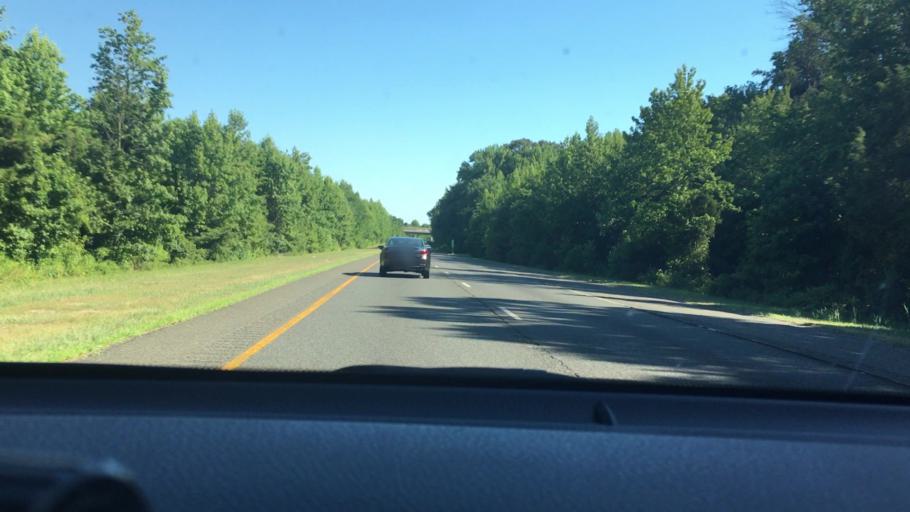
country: US
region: New Jersey
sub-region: Gloucester County
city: Wenonah
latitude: 39.7832
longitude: -75.1164
